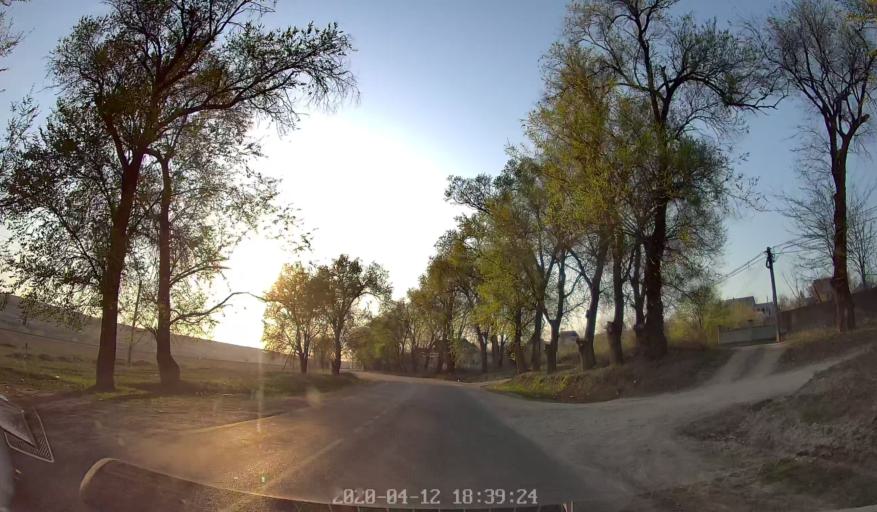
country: MD
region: Chisinau
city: Ciorescu
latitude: 47.1282
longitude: 28.9859
